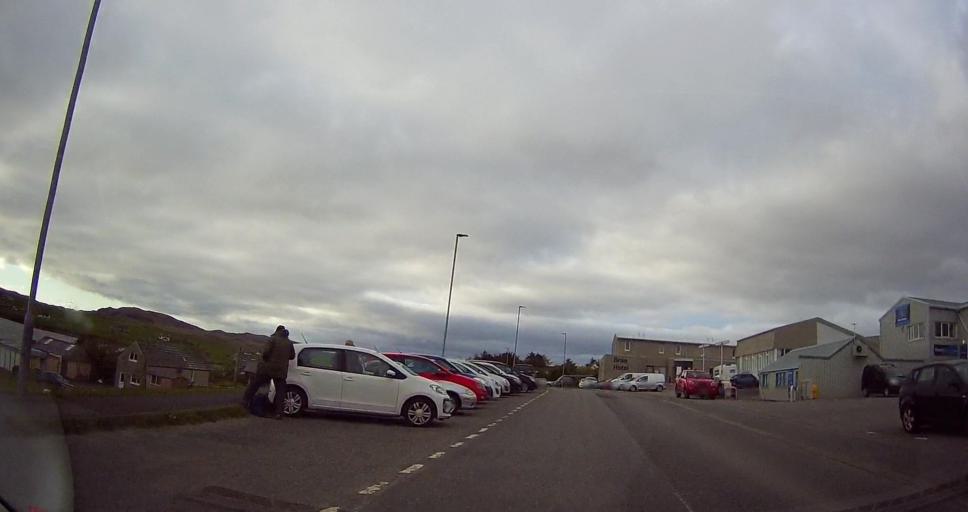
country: GB
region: Scotland
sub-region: Shetland Islands
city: Lerwick
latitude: 60.3906
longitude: -1.3491
